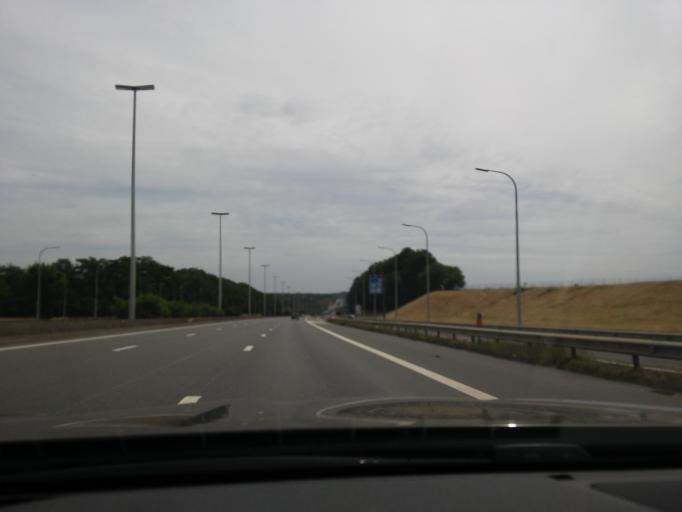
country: BE
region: Flanders
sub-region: Provincie Vlaams-Brabant
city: Bertem
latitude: 50.8565
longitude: 4.6435
